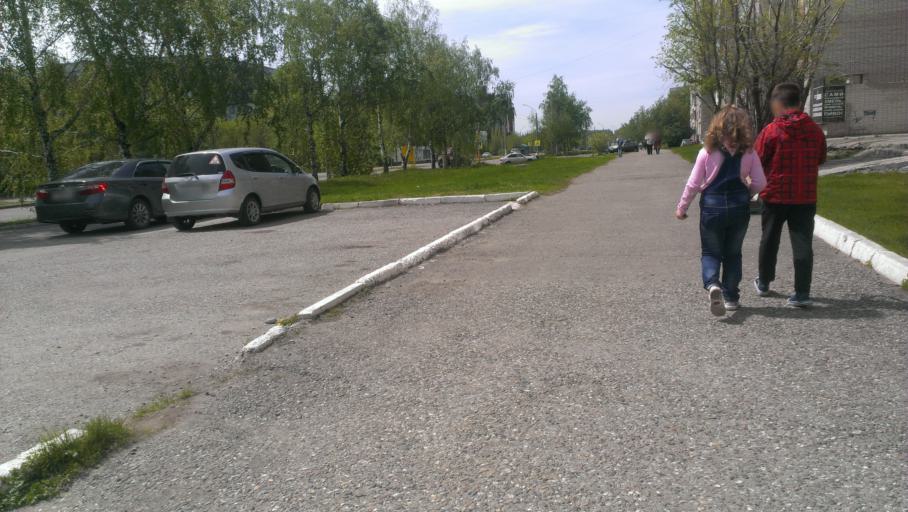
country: RU
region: Altai Krai
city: Novosilikatnyy
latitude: 53.3625
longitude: 83.6732
